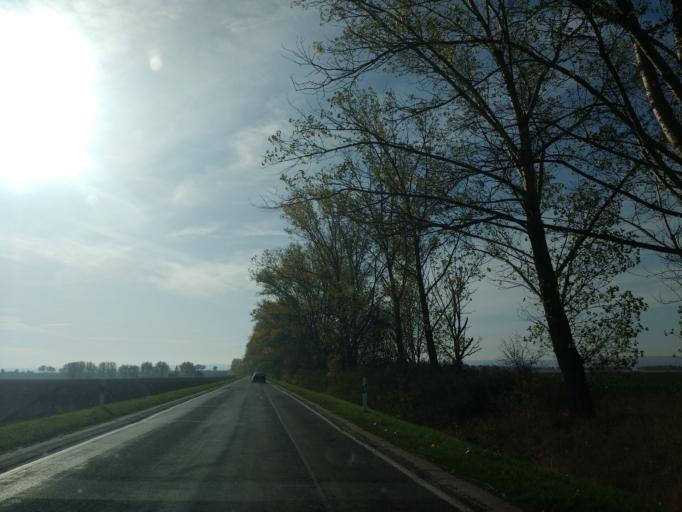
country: DE
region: Thuringia
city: Seebach
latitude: 51.1555
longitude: 10.5184
